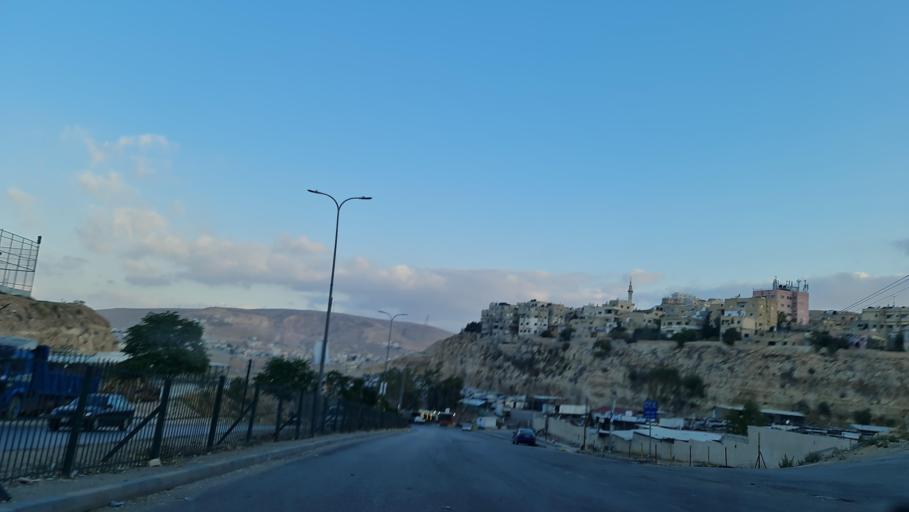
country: JO
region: Zarqa
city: Zarqa
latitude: 32.0787
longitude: 36.0742
